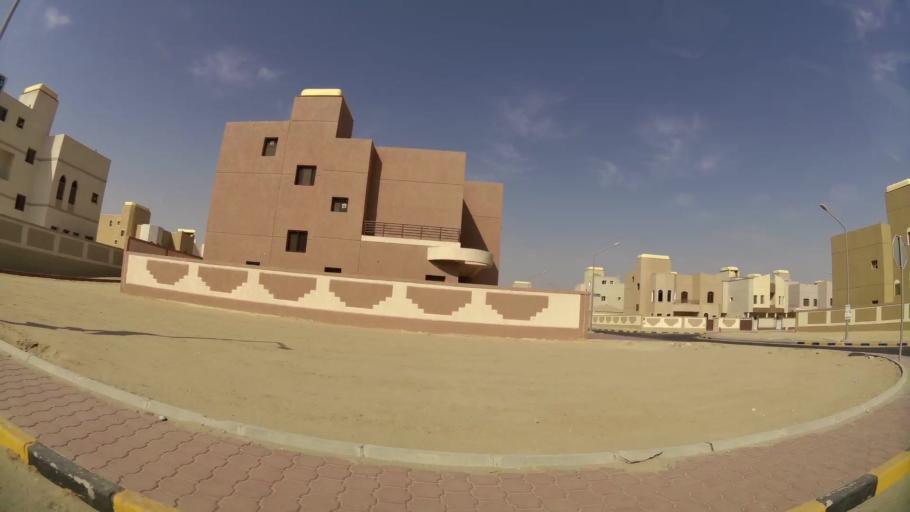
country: KW
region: Al Ahmadi
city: Al Wafrah
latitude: 28.7972
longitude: 48.0747
